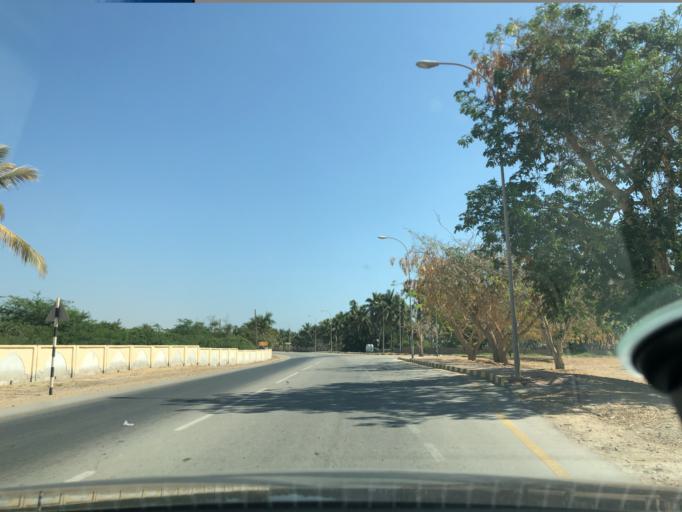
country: OM
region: Zufar
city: Salalah
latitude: 17.0391
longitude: 54.3771
